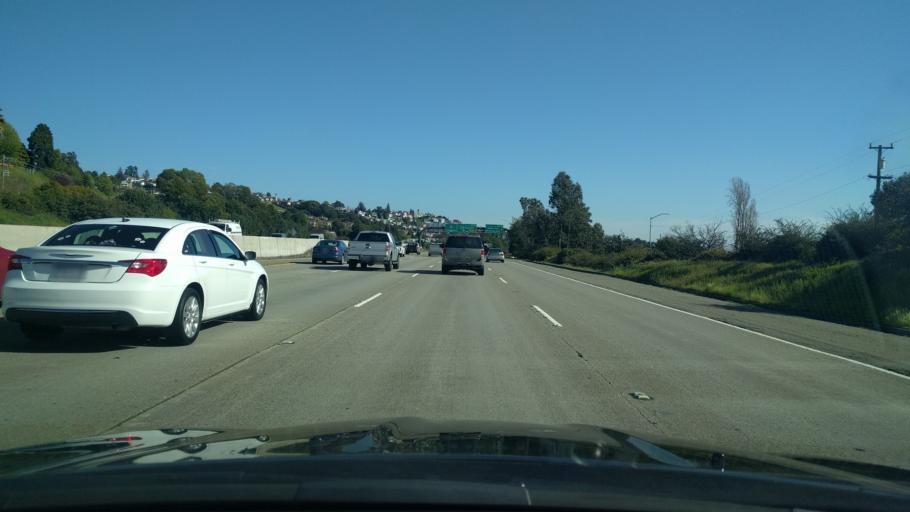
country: US
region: California
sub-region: Alameda County
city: Ashland
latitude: 37.7036
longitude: -122.1143
